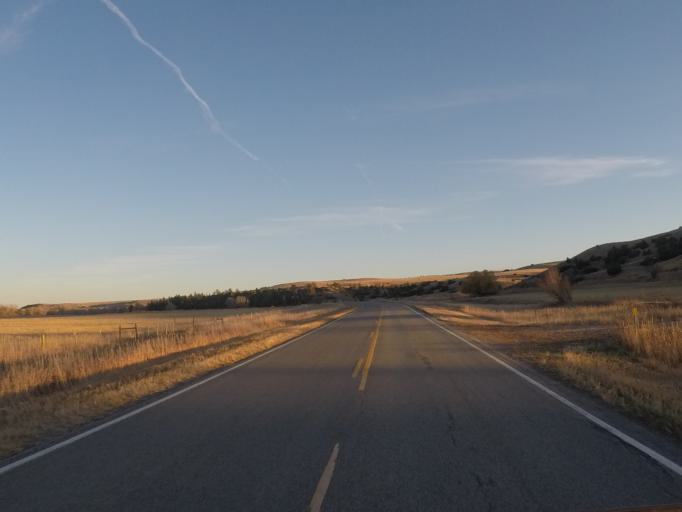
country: US
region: Montana
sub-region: Sweet Grass County
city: Big Timber
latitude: 45.7892
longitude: -109.8522
